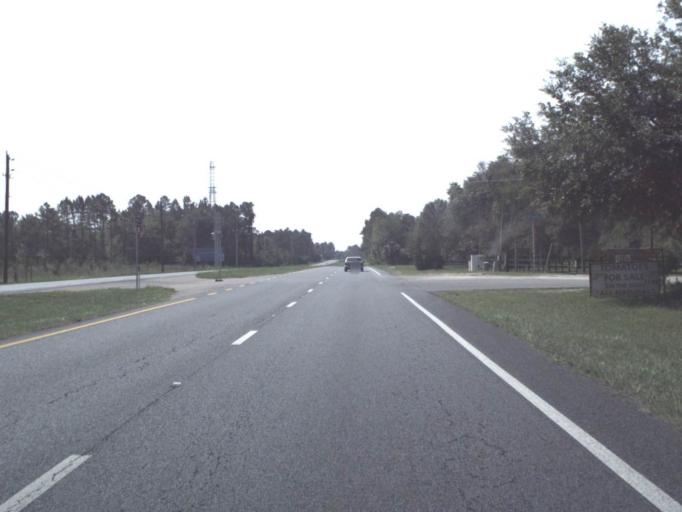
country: US
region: Florida
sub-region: Nassau County
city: Hilliard
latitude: 30.6557
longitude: -81.8780
